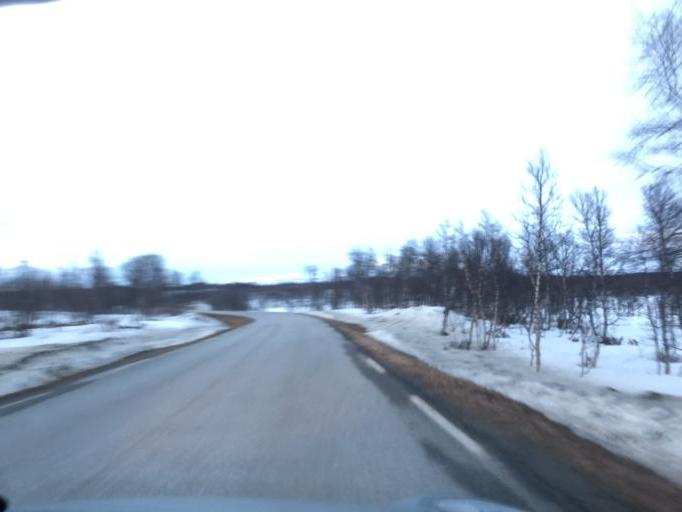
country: NO
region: Sor-Trondelag
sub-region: Tydal
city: Aas
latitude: 62.7221
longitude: 11.8260
